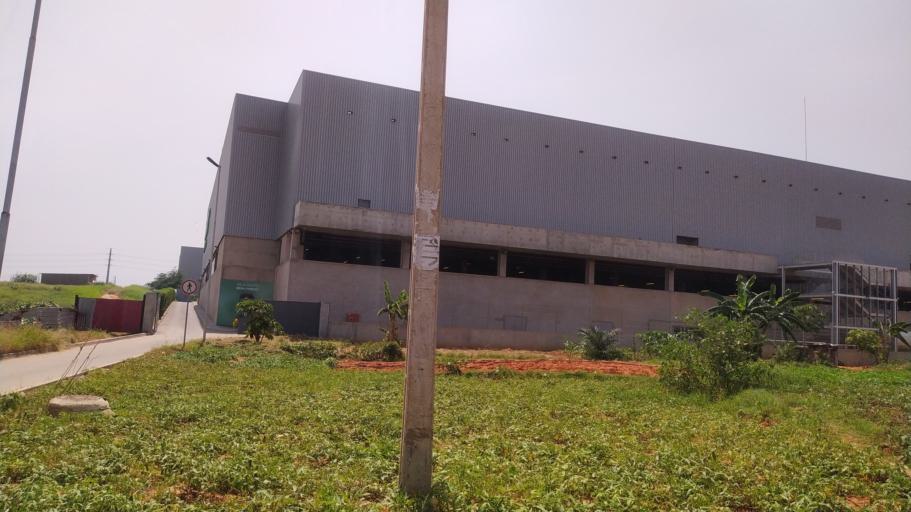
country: AO
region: Luanda
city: Luanda
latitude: -8.8988
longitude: 13.2249
